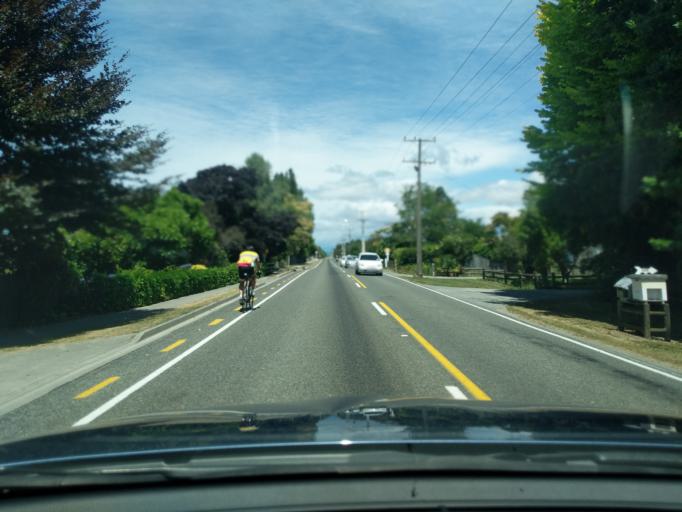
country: NZ
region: Tasman
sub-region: Tasman District
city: Motueka
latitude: -41.0780
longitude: 172.9974
